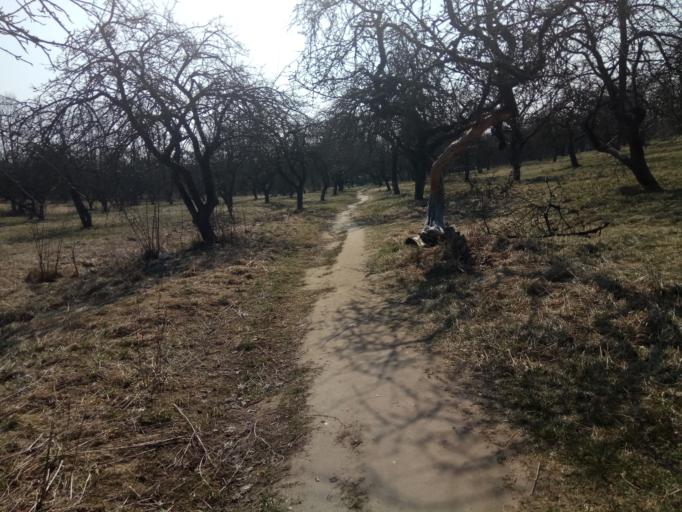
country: BY
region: Minsk
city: Valozhyn
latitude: 54.0840
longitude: 26.5173
